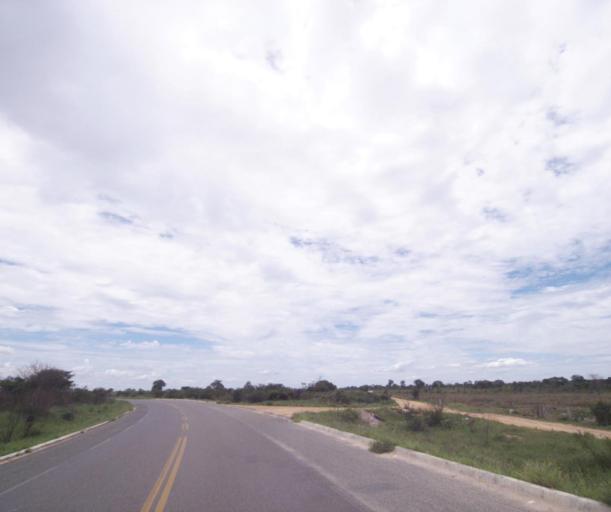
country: BR
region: Bahia
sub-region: Carinhanha
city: Carinhanha
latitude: -14.2902
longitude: -43.7855
